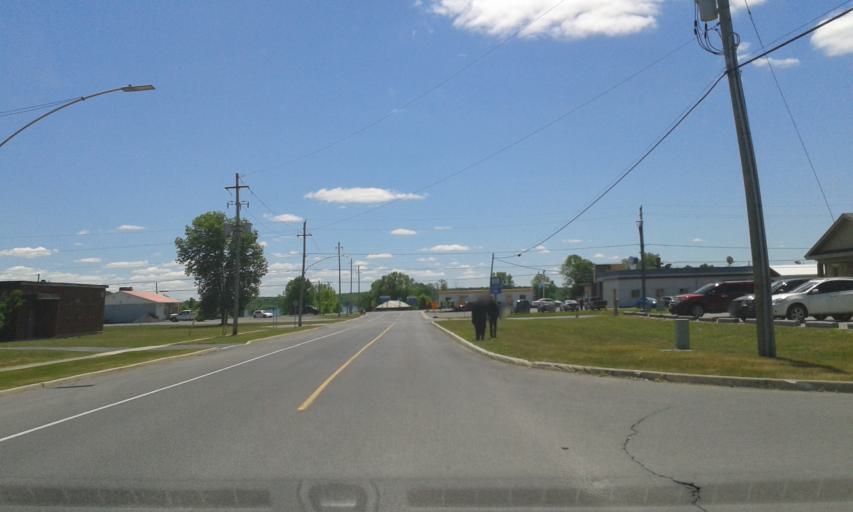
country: US
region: New York
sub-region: St. Lawrence County
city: Massena
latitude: 44.9972
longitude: -74.9878
